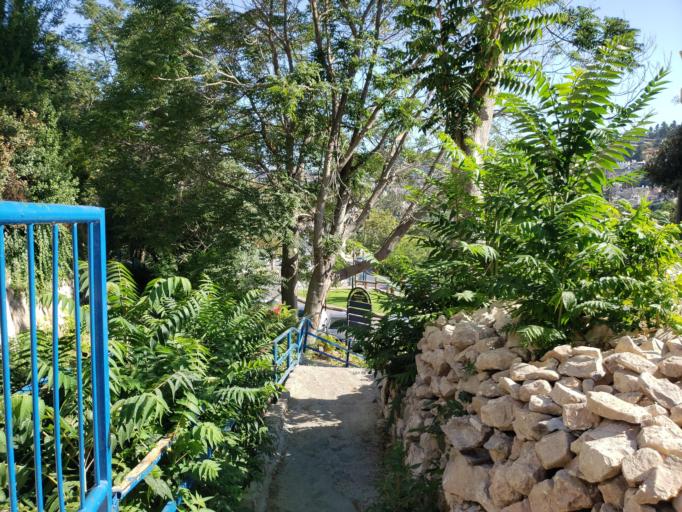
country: IL
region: Northern District
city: Safed
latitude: 32.9659
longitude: 35.4968
